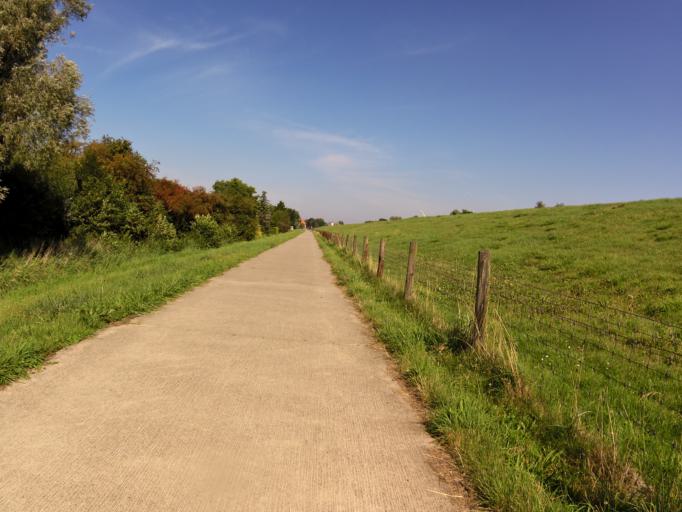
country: DE
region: Lower Saxony
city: Brake (Unterweser)
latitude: 53.2983
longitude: 8.4859
